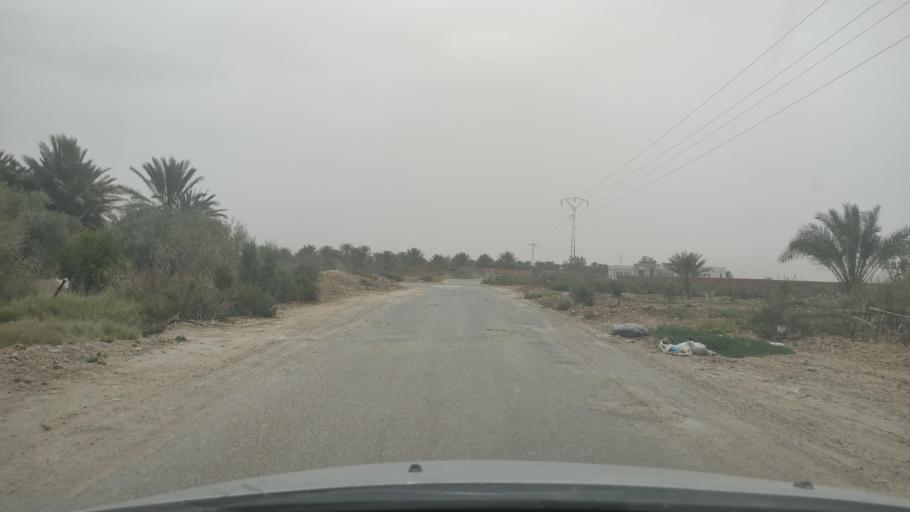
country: TN
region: Gafsa
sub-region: Gafsa Municipality
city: Gafsa
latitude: 34.3247
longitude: 8.9519
